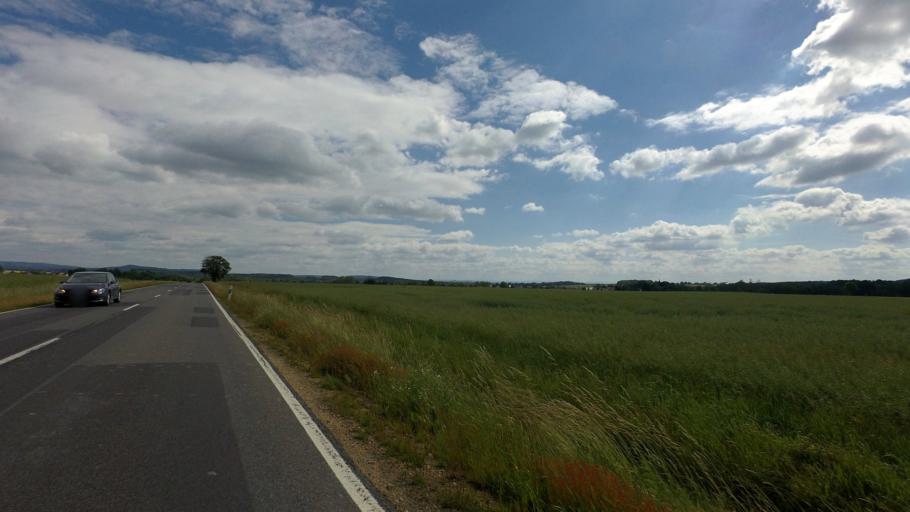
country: DE
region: Saxony
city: Rammenau
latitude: 51.1603
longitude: 14.1435
